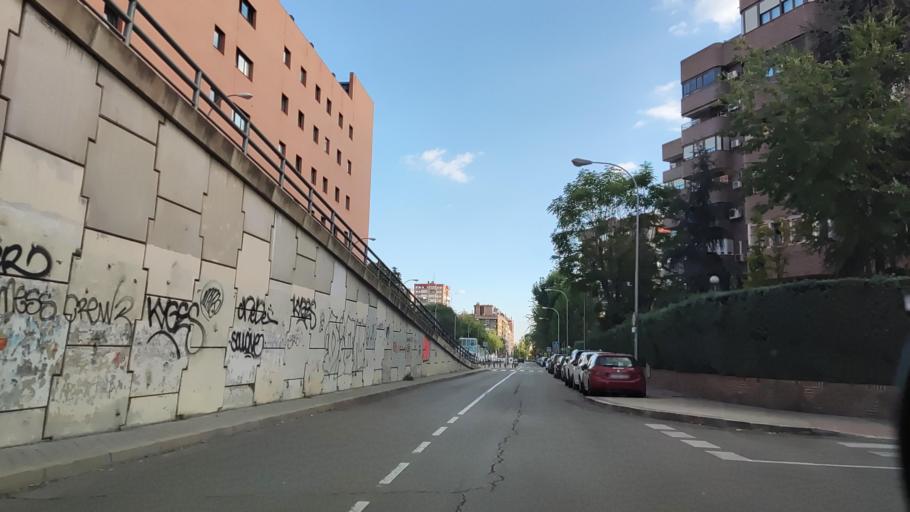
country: ES
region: Madrid
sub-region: Provincia de Madrid
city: Arganzuela
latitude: 40.4011
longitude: -3.7067
